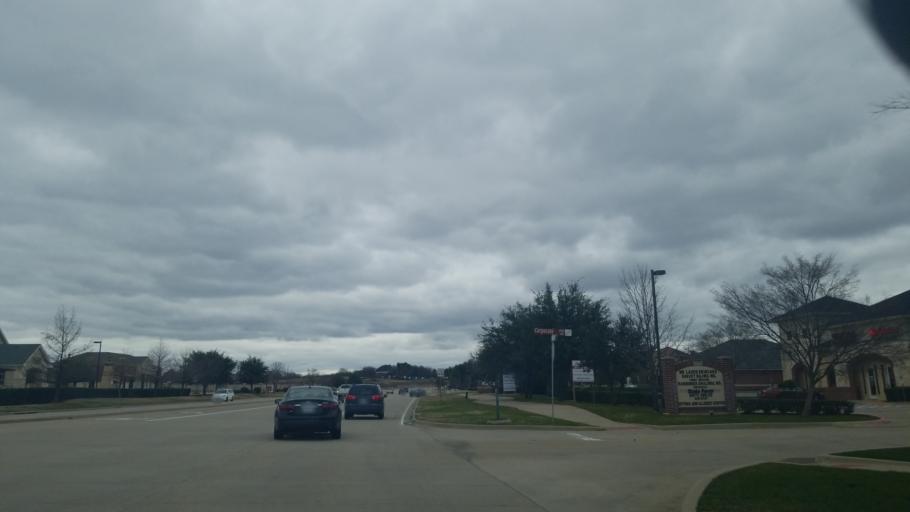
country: US
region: Texas
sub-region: Denton County
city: Double Oak
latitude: 33.0520
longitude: -97.0738
